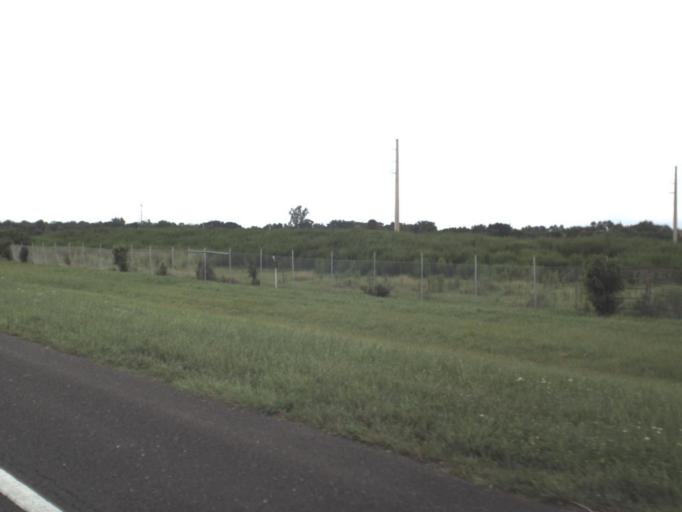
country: US
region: Florida
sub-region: Manatee County
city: Samoset
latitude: 27.4602
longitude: -82.5302
